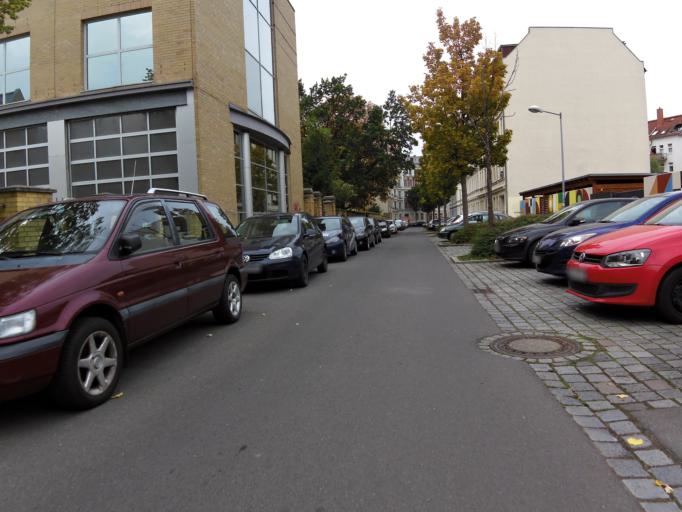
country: DE
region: Saxony
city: Leipzig
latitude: 51.3294
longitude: 12.3333
